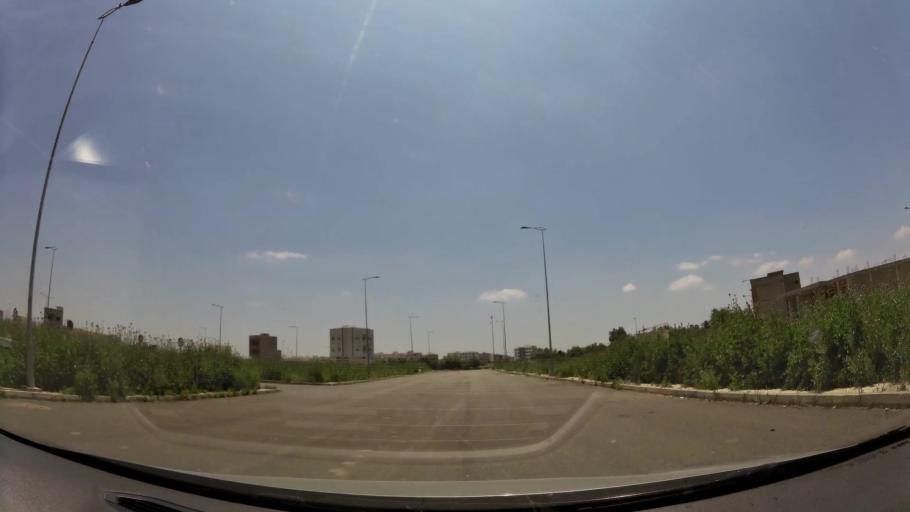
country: MA
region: Fes-Boulemane
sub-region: Fes
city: Fes
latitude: 34.0281
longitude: -5.0528
